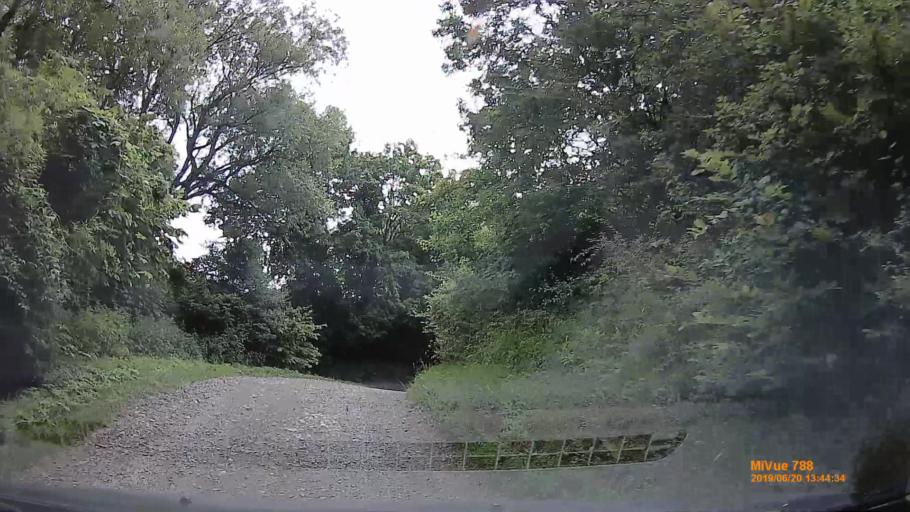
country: HU
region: Baranya
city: Hosszuheteny
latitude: 46.1773
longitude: 18.3491
